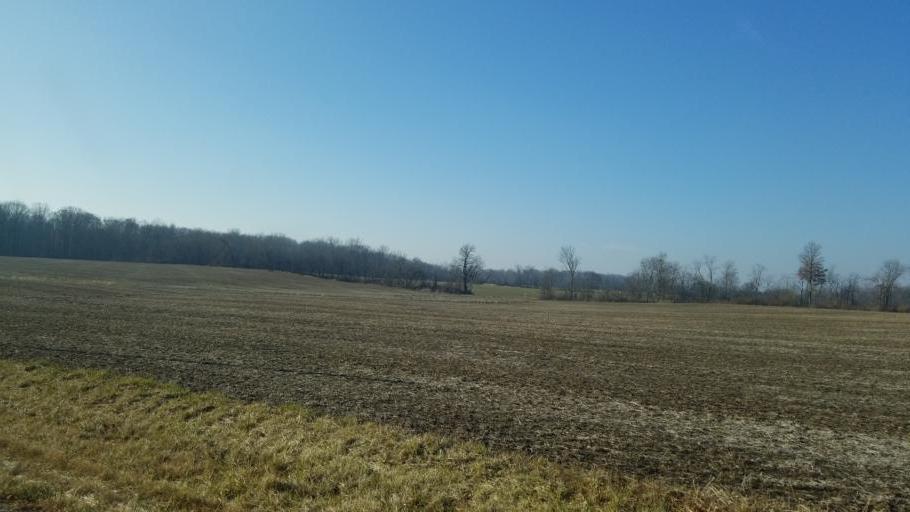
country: US
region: Ohio
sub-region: Seneca County
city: Tiffin
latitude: 41.1217
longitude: -83.1121
